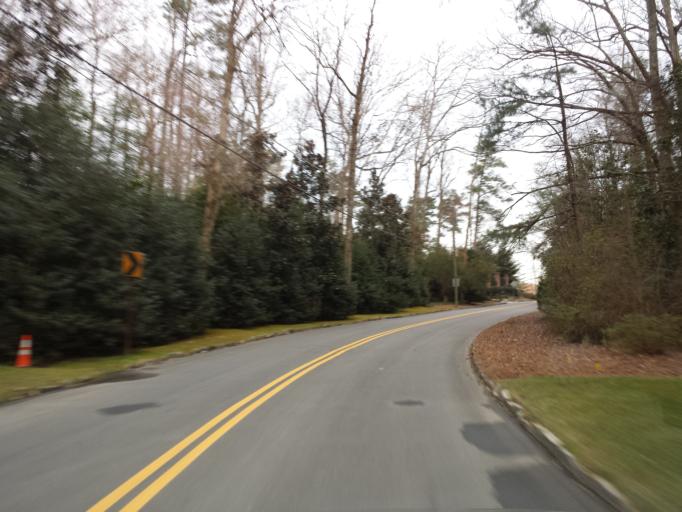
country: US
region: Georgia
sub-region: Cobb County
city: Vinings
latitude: 33.8835
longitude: -84.4185
